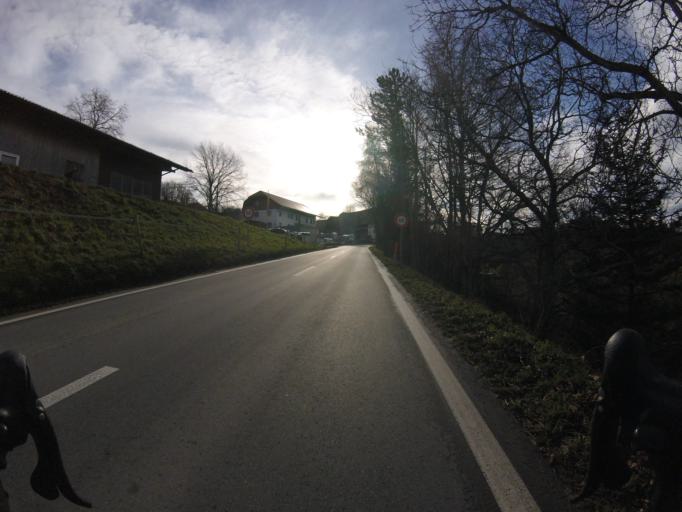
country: CH
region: Fribourg
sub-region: Sense District
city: Ueberstorf
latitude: 46.8587
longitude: 7.3157
